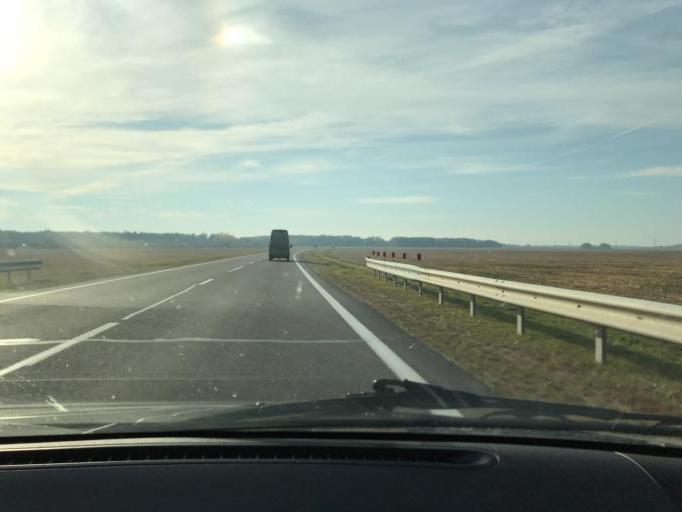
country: BY
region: Brest
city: Horad Pinsk
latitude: 52.1490
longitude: 25.9137
